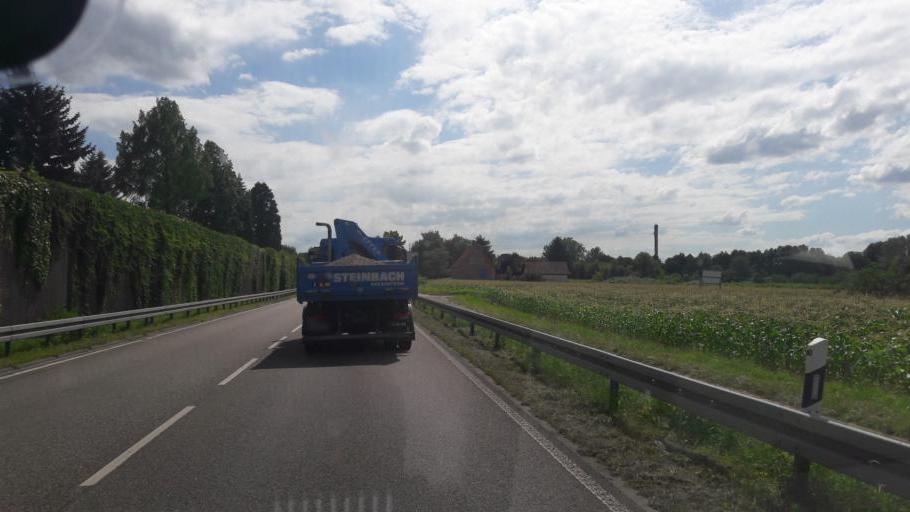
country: DE
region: Baden-Wuerttemberg
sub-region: Karlsruhe Region
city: Weingarten
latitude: 49.0141
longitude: 8.4919
